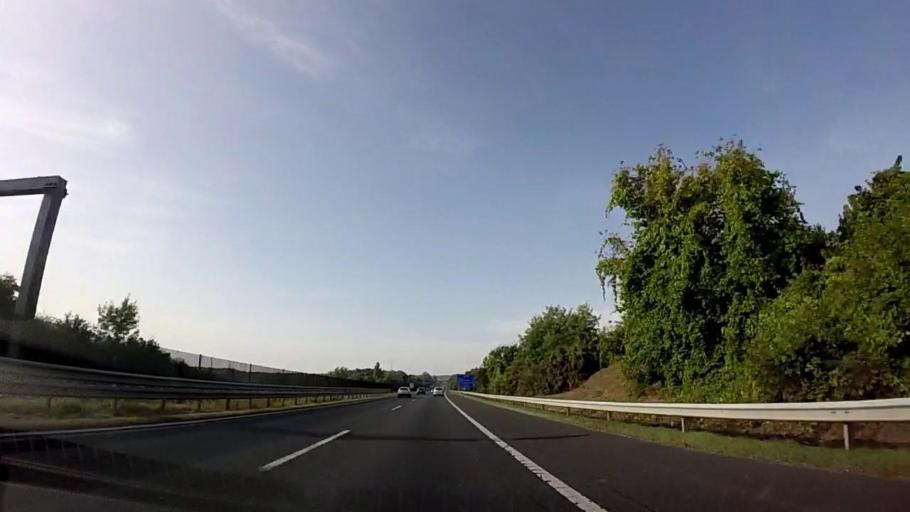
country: HU
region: Fejer
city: Martonvasar
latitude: 47.3265
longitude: 18.7708
